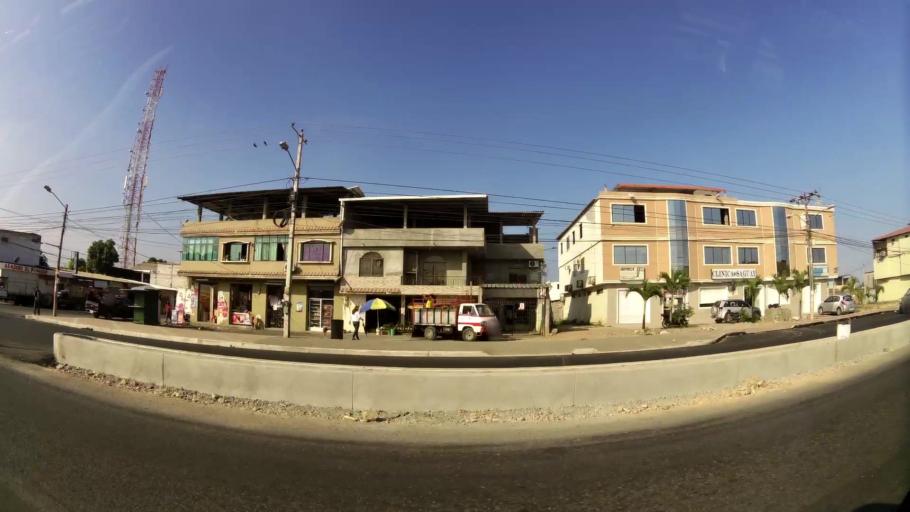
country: EC
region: Guayas
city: Eloy Alfaro
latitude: -2.1801
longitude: -79.8453
